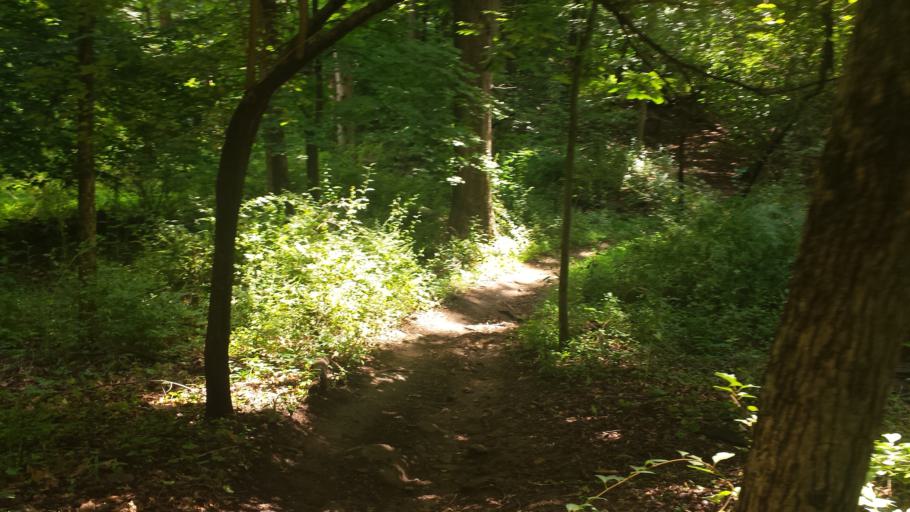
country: US
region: New York
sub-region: Westchester County
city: Hawthorne
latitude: 41.1142
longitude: -73.7968
